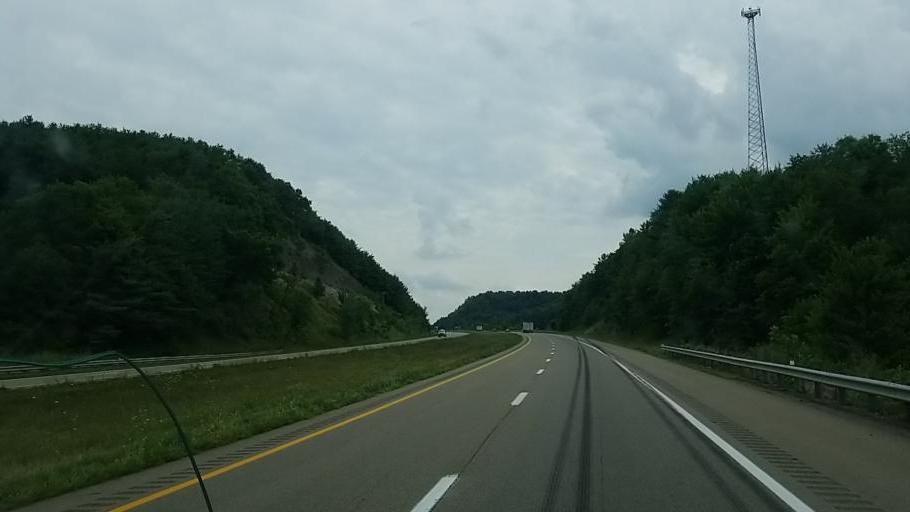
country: US
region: Ohio
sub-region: Tuscarawas County
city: Newcomerstown
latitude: 40.3190
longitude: -81.5700
